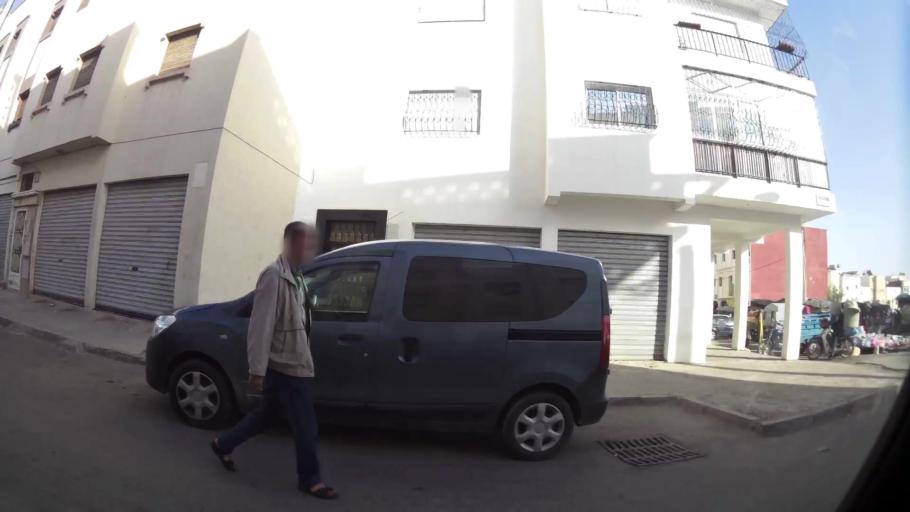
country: MA
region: Oued ed Dahab-Lagouira
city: Dakhla
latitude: 30.4002
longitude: -9.5493
